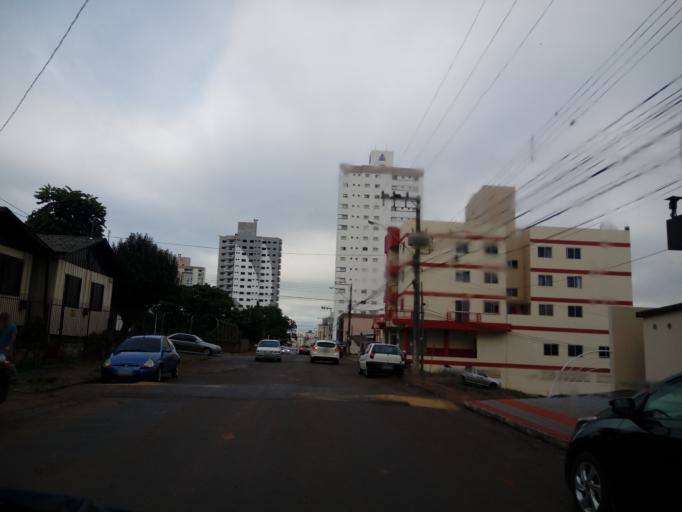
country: BR
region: Santa Catarina
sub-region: Chapeco
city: Chapeco
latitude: -27.0906
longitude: -52.6127
